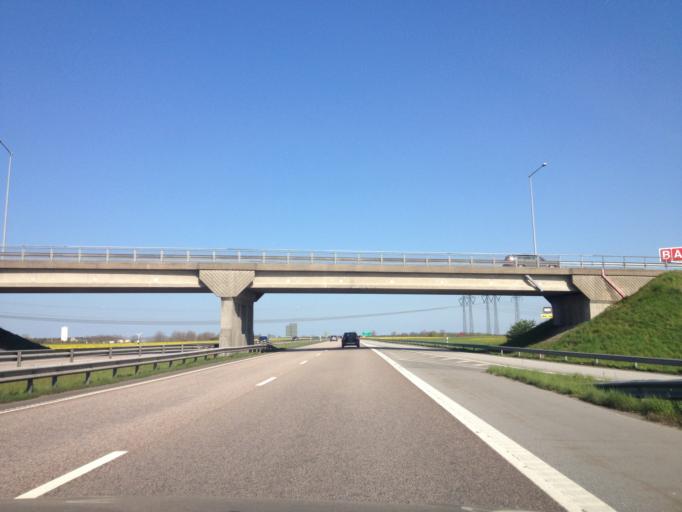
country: SE
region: Skane
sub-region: Kavlinge Kommun
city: Hofterup
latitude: 55.7679
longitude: 12.9847
